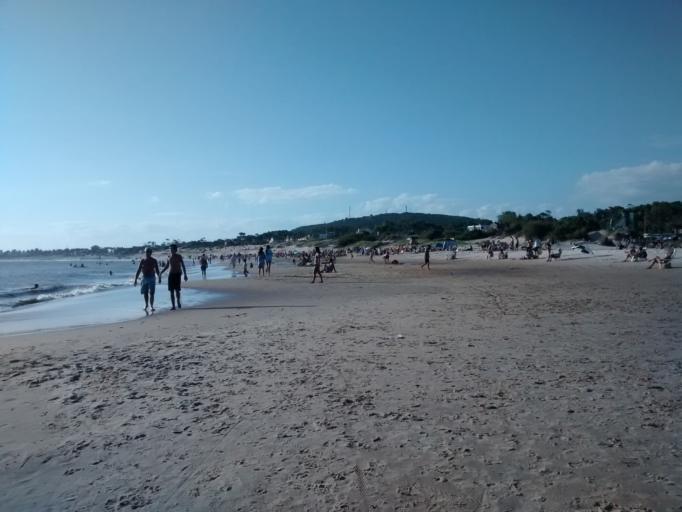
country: UY
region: Maldonado
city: Piriapolis
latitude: -34.8945
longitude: -55.2607
